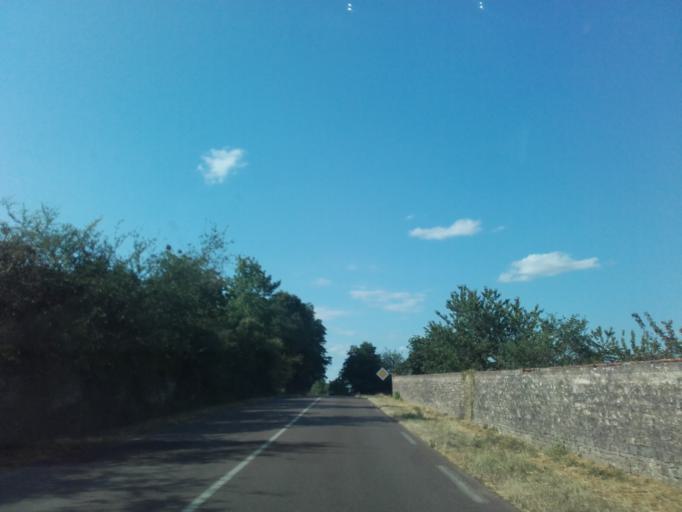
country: FR
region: Bourgogne
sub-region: Departement de Saone-et-Loire
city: Fontaines
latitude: 46.8507
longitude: 4.7545
